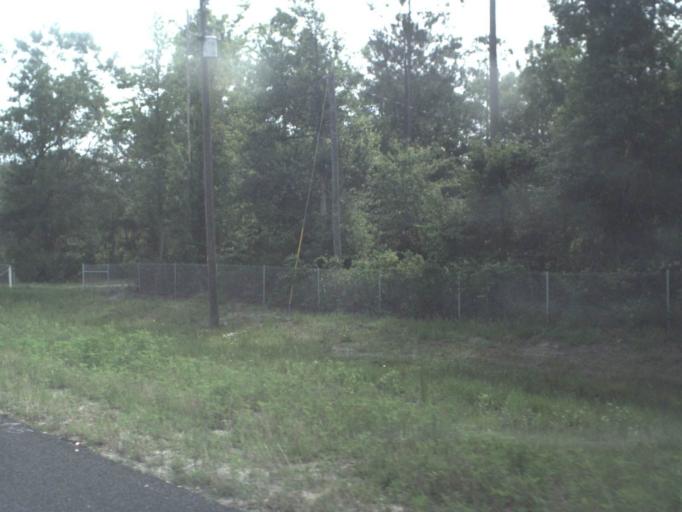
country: US
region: Florida
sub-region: Nassau County
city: Nassau Village-Ratliff
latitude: 30.4561
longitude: -81.9135
